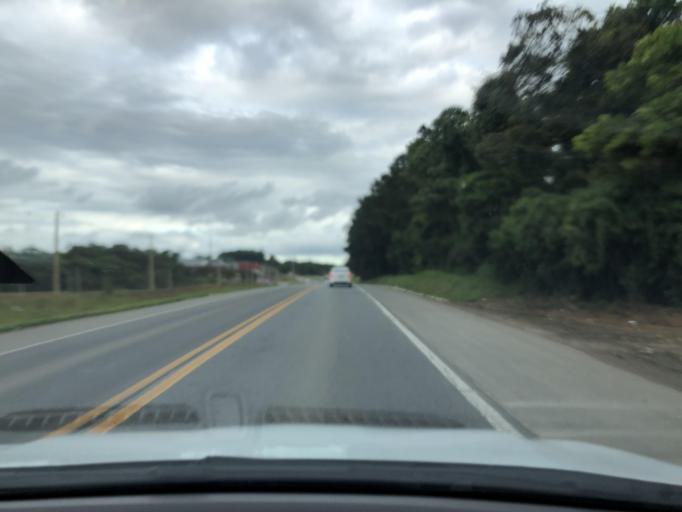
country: BR
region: Santa Catarina
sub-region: Joinville
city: Joinville
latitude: -26.4274
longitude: -48.7908
